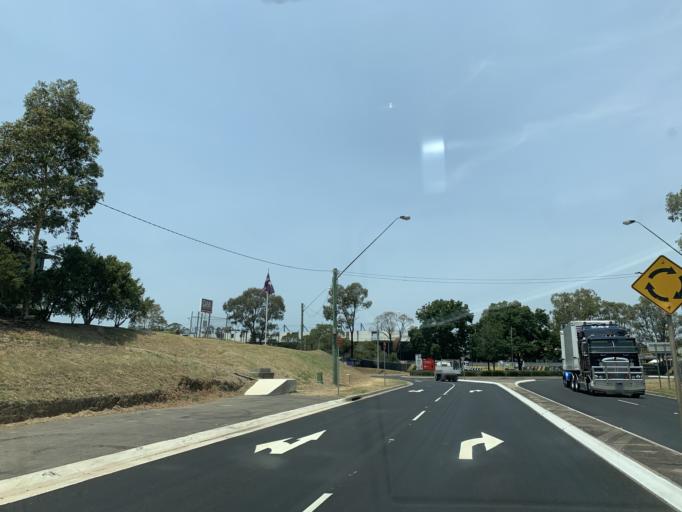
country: AU
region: New South Wales
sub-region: Blacktown
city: Doonside
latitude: -33.8016
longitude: 150.8700
